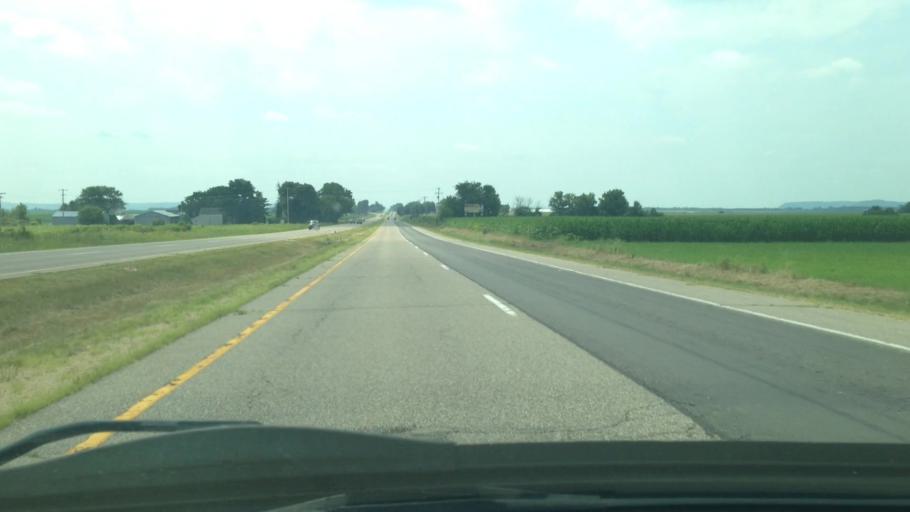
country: US
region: Wisconsin
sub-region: Sauk County
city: Prairie du Sac
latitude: 43.3319
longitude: -89.7591
